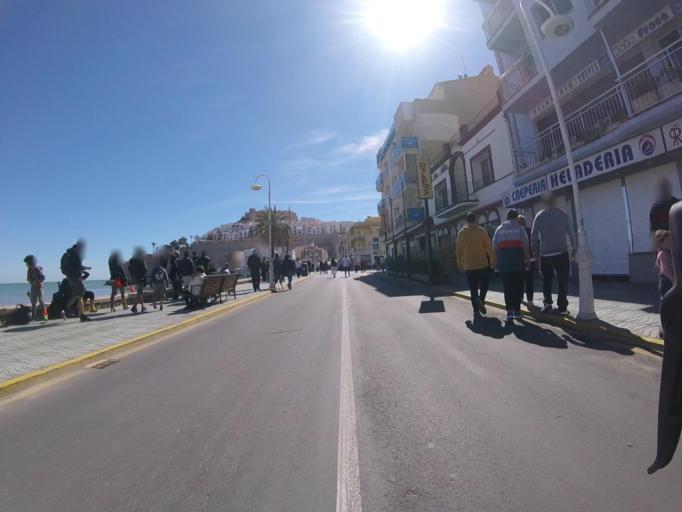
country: ES
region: Valencia
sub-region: Provincia de Castello
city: Peniscola
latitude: 40.3597
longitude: 0.4042
